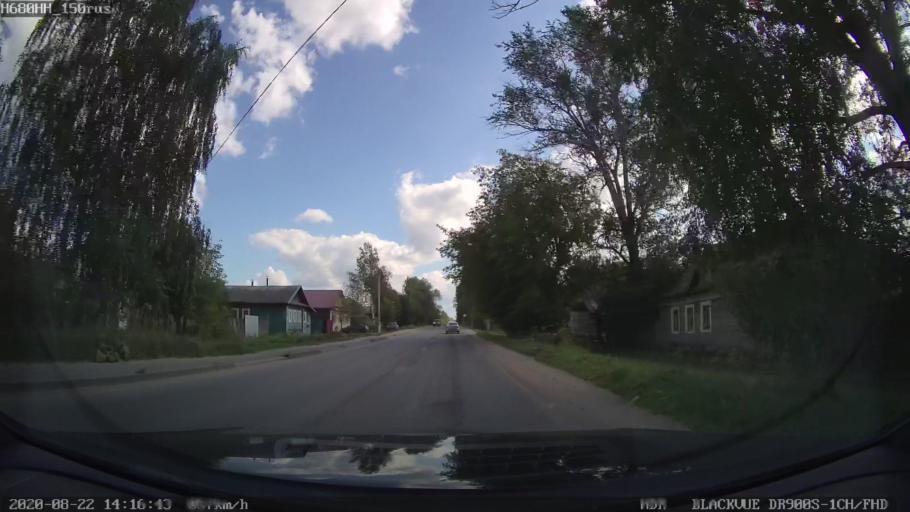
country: RU
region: Tverskaya
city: Bezhetsk
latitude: 57.7744
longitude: 36.6994
